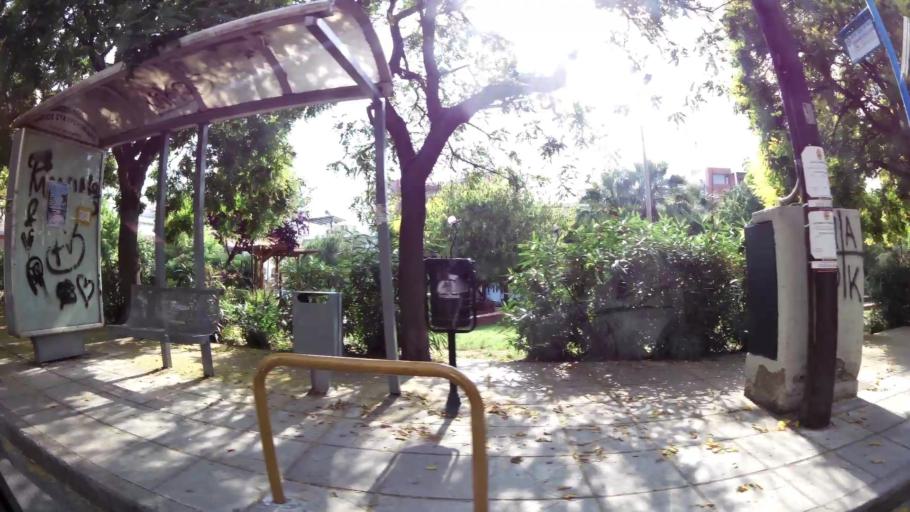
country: GR
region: Central Macedonia
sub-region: Nomos Thessalonikis
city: Stavroupoli
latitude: 40.6686
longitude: 22.9279
